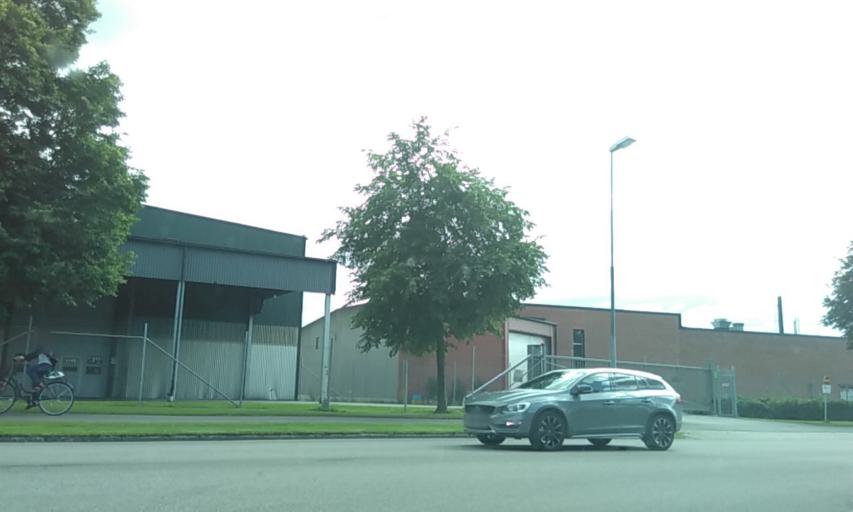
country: SE
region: Vaestra Goetaland
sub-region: Skara Kommun
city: Skara
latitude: 58.3849
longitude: 13.4489
